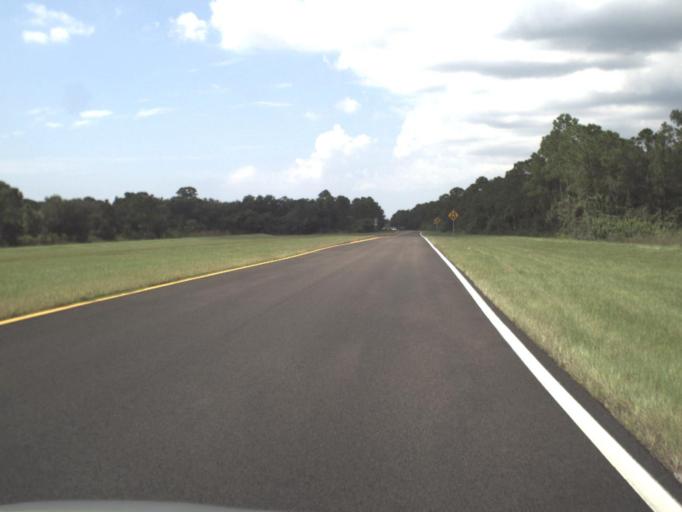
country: US
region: Florida
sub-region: Sarasota County
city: Warm Mineral Springs
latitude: 27.0475
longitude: -82.3048
